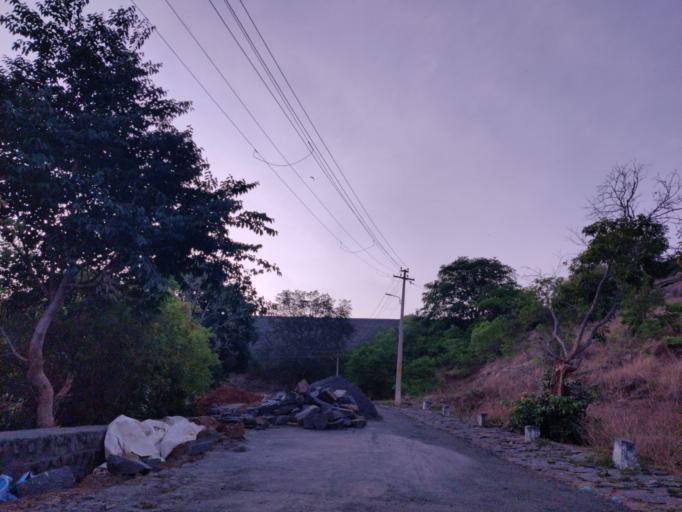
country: IN
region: Tamil Nadu
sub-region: Salem
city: Salem
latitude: 11.6212
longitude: 78.1506
